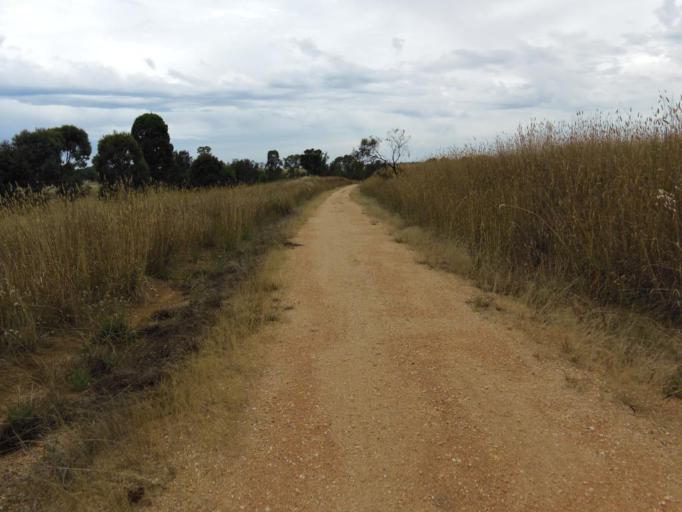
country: AU
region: Victoria
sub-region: Greater Bendigo
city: Kennington
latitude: -36.8586
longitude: 144.6219
